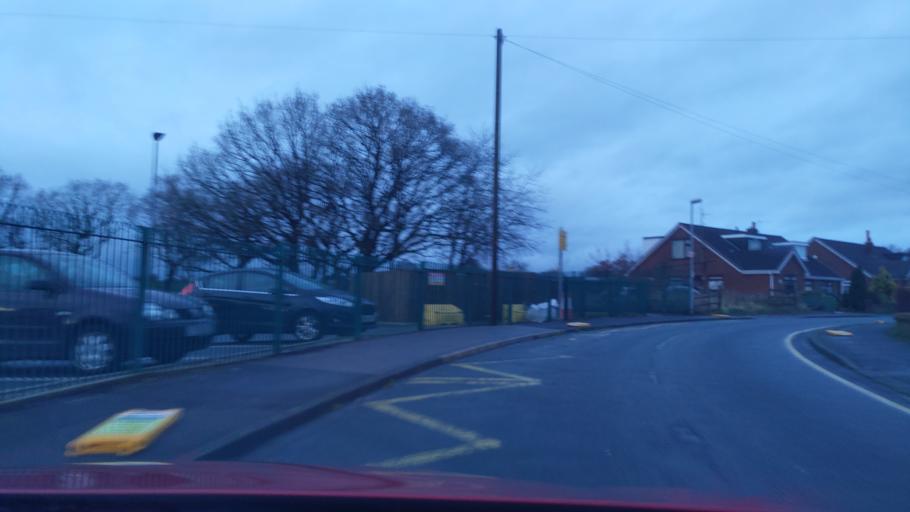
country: GB
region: England
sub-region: Lancashire
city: Euxton
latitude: 53.6704
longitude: -2.6832
